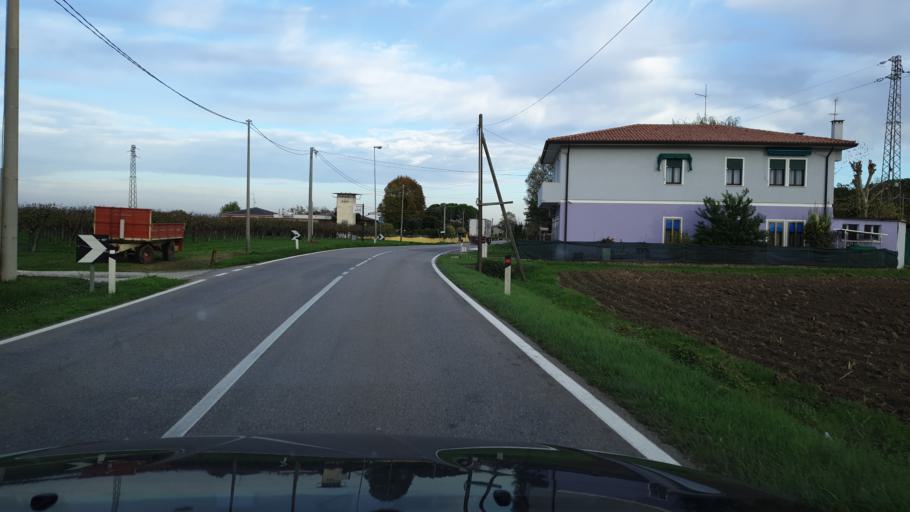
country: IT
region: Veneto
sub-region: Provincia di Padova
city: Pernumia
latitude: 45.2317
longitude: 11.7932
